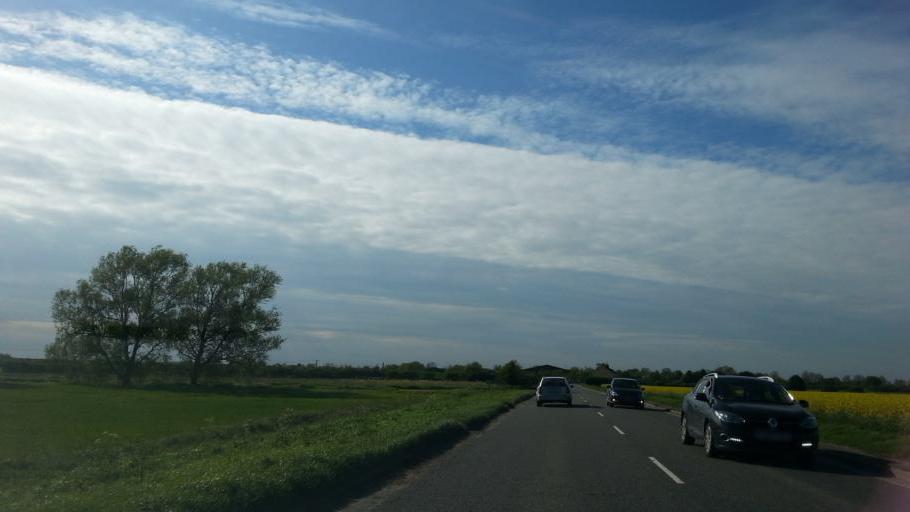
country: GB
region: England
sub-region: Cambridgeshire
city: Chatteris
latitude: 52.4425
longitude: 0.0680
